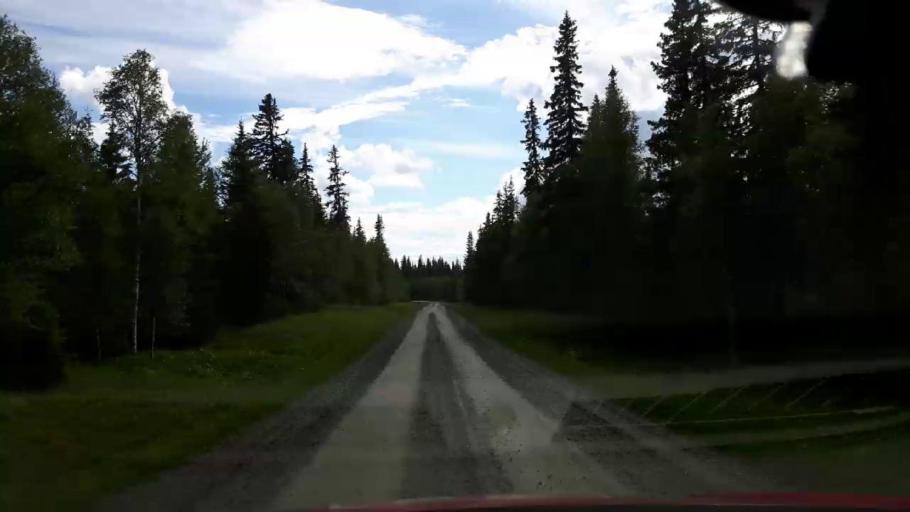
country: SE
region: Jaemtland
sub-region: Krokoms Kommun
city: Valla
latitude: 63.8604
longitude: 14.1024
